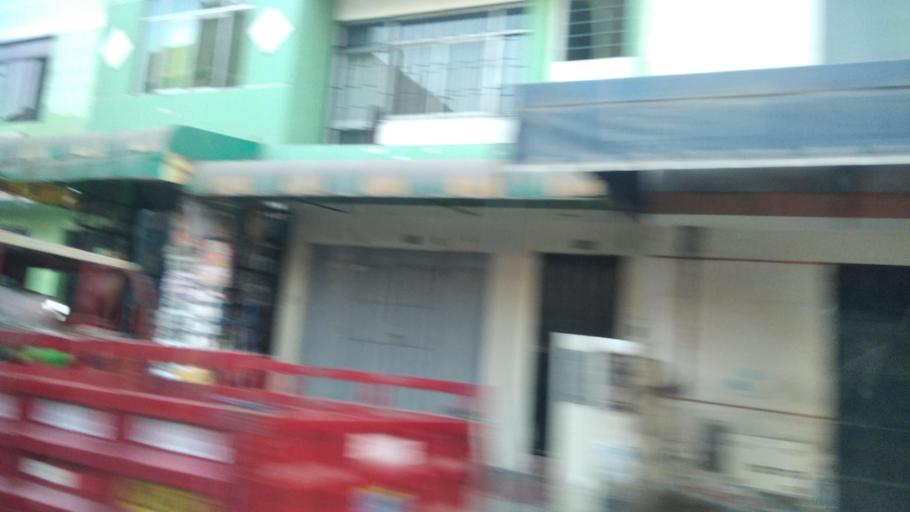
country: PE
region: Lima
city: Lima
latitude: -12.0134
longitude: -77.0081
